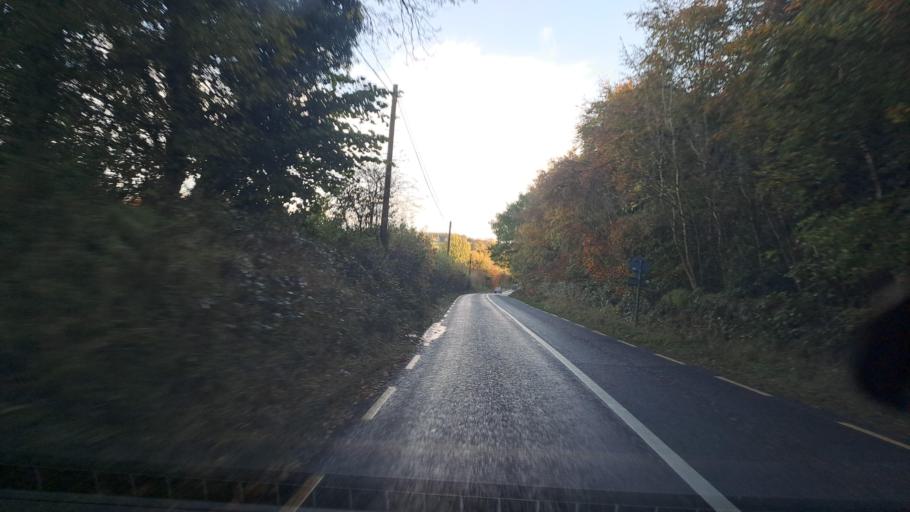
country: IE
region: Ulster
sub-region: An Cabhan
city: Cootehill
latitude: 54.1085
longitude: -7.0536
